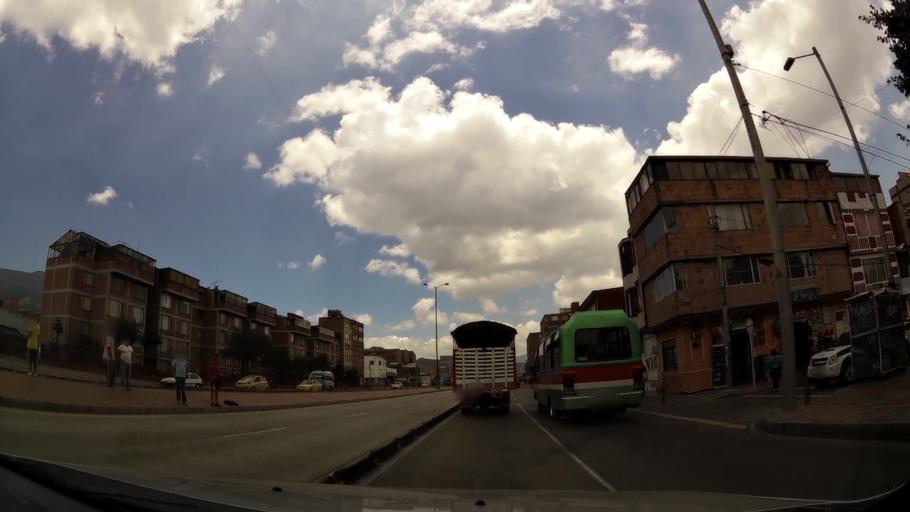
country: CO
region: Bogota D.C.
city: Bogota
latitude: 4.5854
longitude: -74.0875
